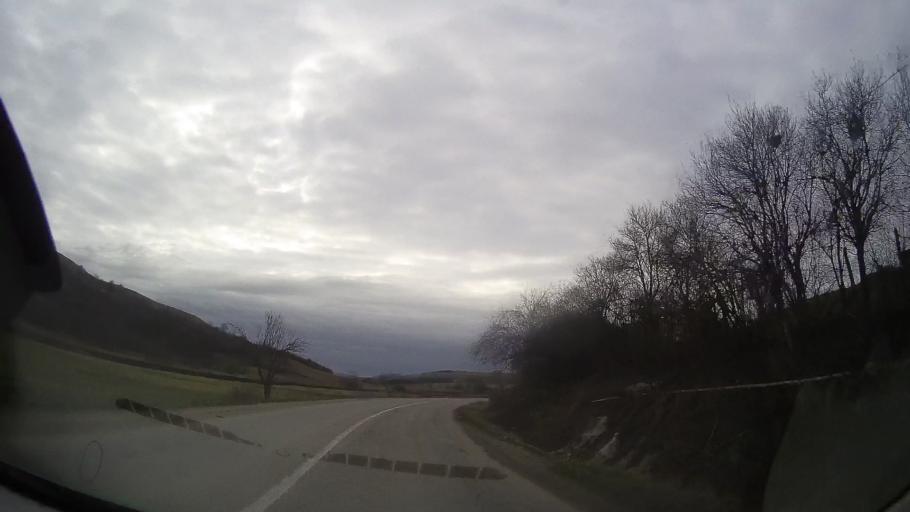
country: RO
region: Bistrita-Nasaud
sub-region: Comuna Budesti
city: Budesti
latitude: 46.8655
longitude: 24.2463
